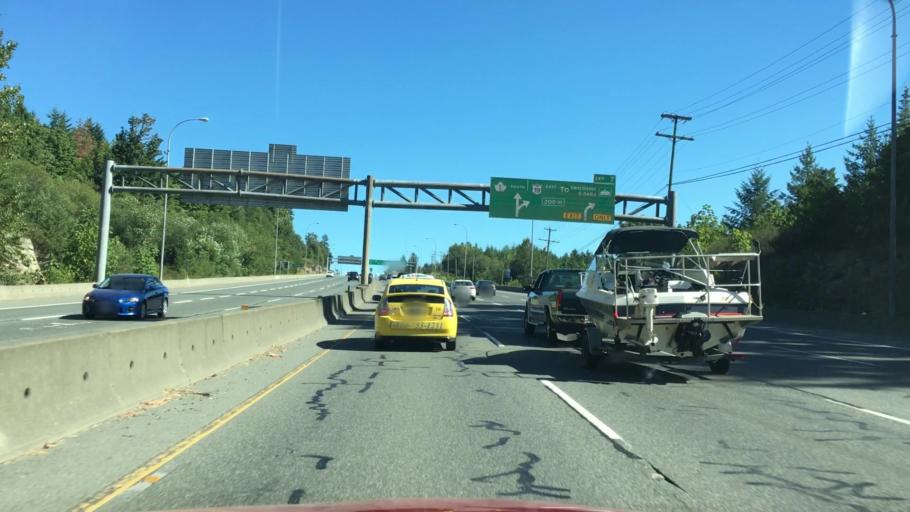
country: CA
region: British Columbia
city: Nanaimo
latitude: 49.1185
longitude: -123.9122
